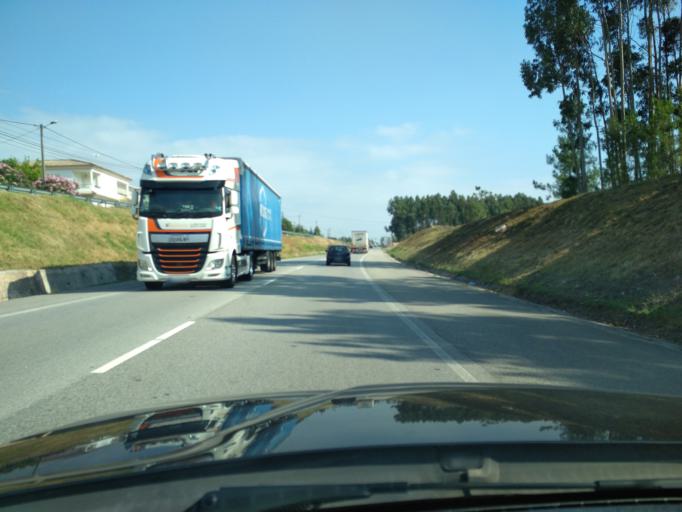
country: PT
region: Aveiro
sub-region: Mealhada
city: Pampilhosa do Botao
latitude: 40.3161
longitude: -8.4516
